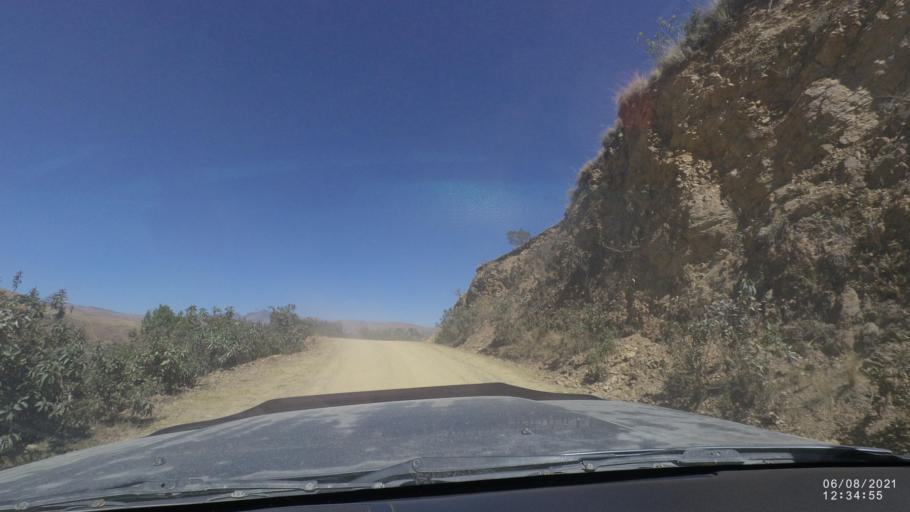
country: BO
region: Cochabamba
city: Colchani
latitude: -16.7777
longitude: -66.6466
